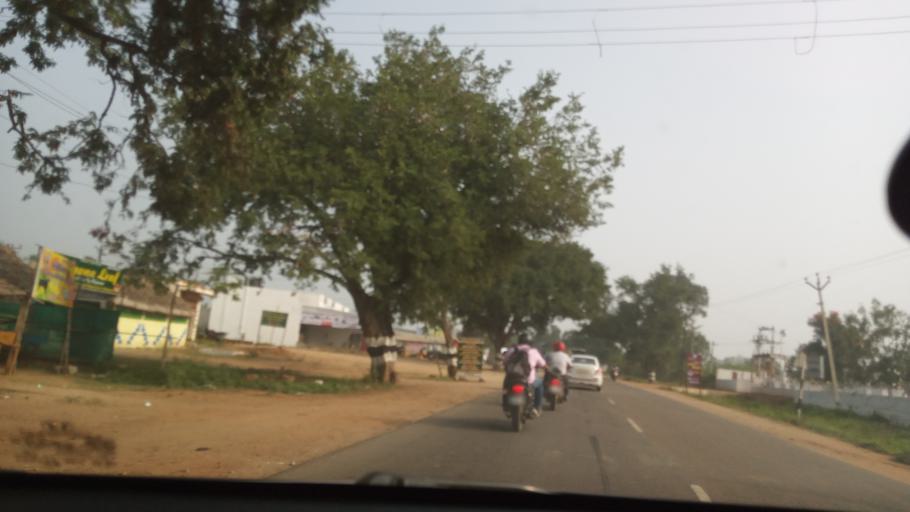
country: IN
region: Tamil Nadu
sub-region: Coimbatore
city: Annur
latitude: 11.1609
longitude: 77.0512
